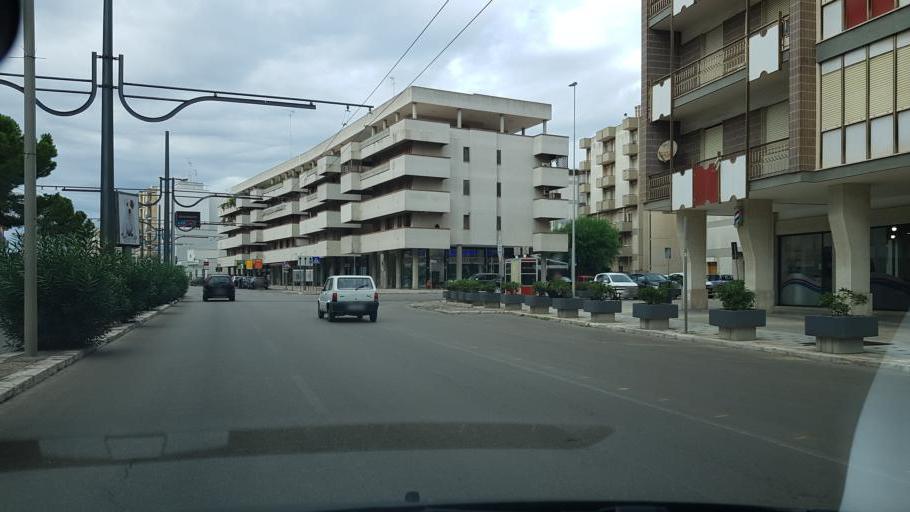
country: IT
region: Apulia
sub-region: Provincia di Lecce
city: Lecce
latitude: 40.3614
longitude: 18.1795
